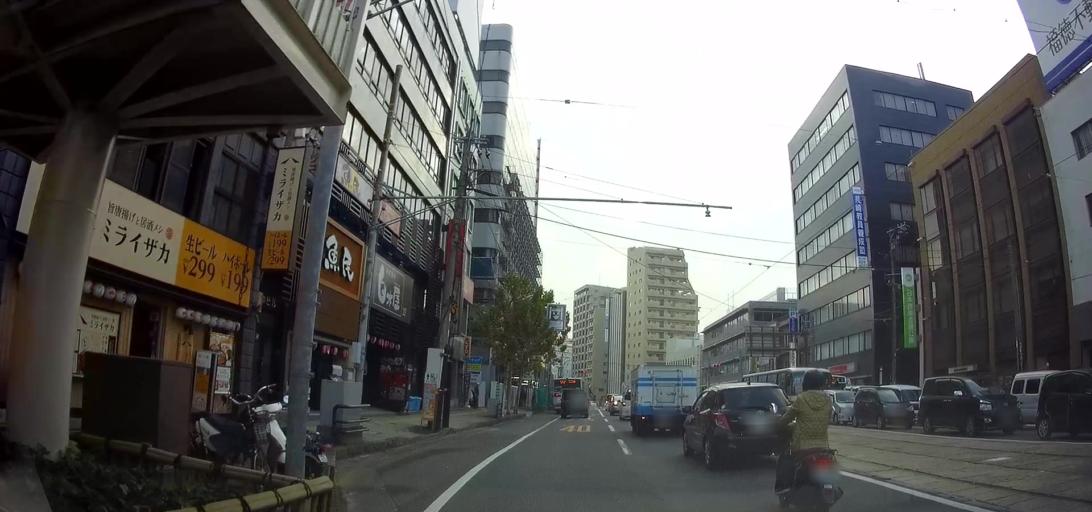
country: JP
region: Nagasaki
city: Nagasaki-shi
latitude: 32.7522
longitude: 129.8723
